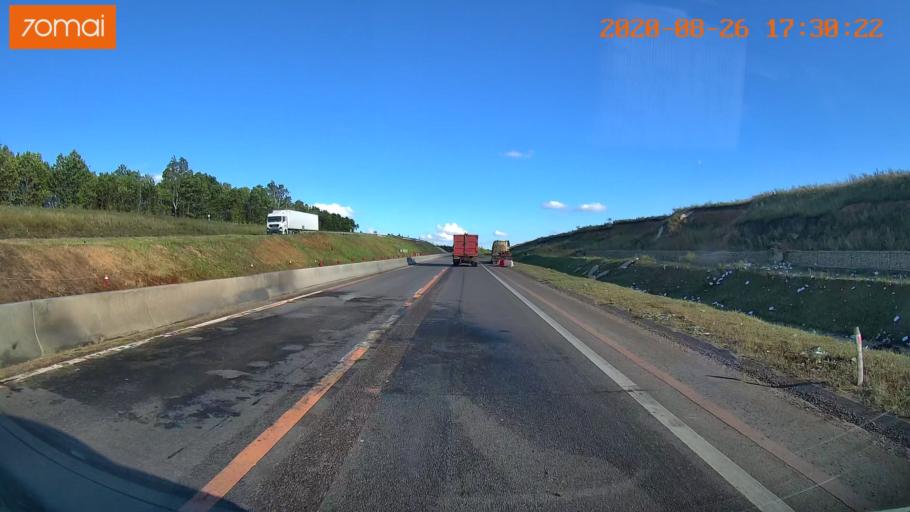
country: RU
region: Tula
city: Kazachka
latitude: 53.4455
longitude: 38.1678
